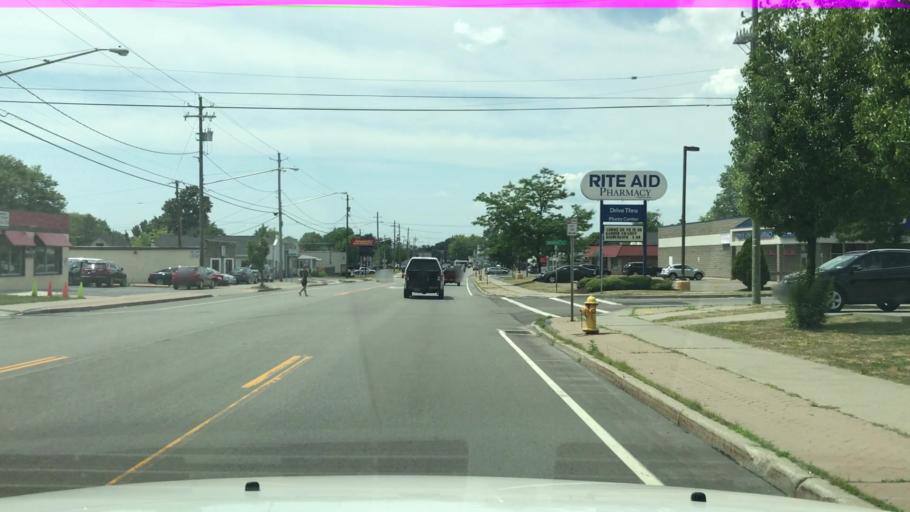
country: US
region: New York
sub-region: Erie County
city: Depew
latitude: 42.9017
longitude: -78.6928
